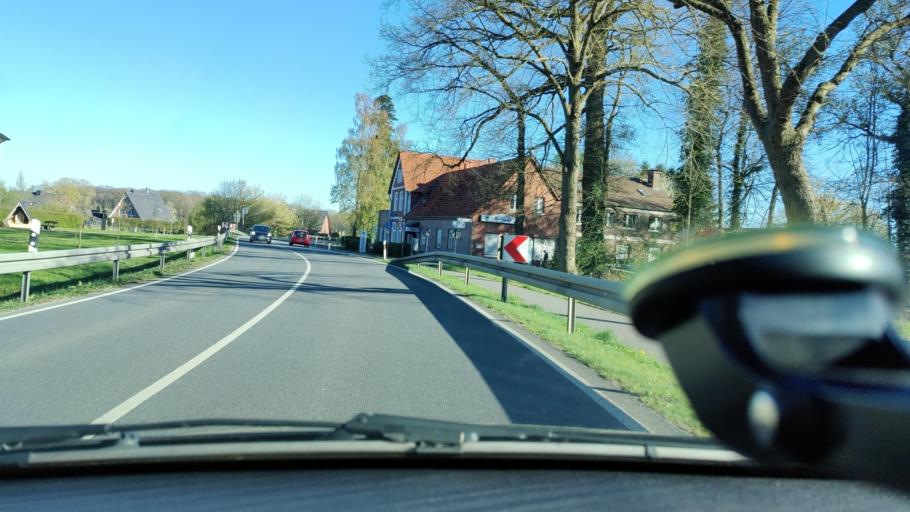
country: DE
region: North Rhine-Westphalia
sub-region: Regierungsbezirk Munster
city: Coesfeld
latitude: 51.9667
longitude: 7.1578
